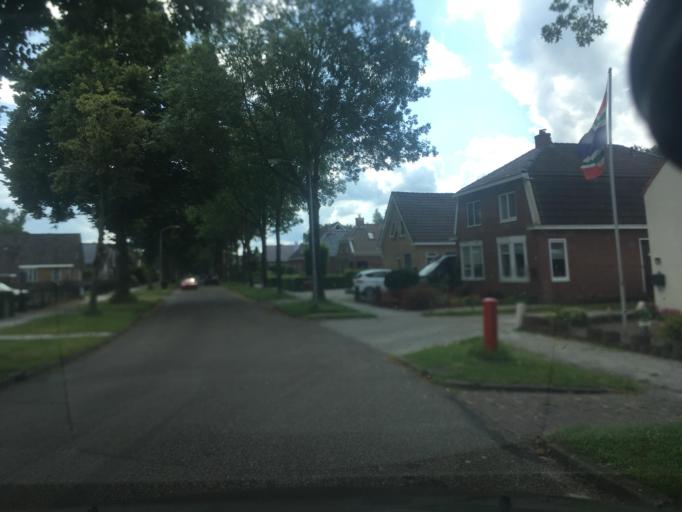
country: NL
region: Groningen
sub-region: Gemeente Hoogezand-Sappemeer
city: Sappemeer
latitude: 53.1590
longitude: 6.7865
